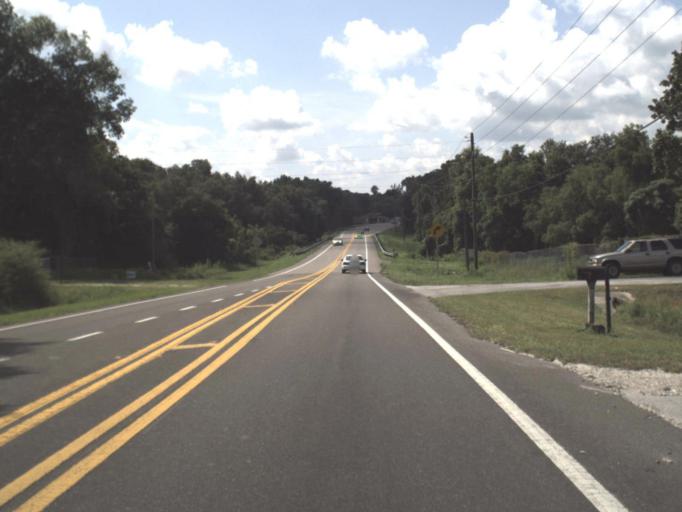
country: US
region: Florida
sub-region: Citrus County
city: Floral City
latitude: 28.7809
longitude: -82.2966
